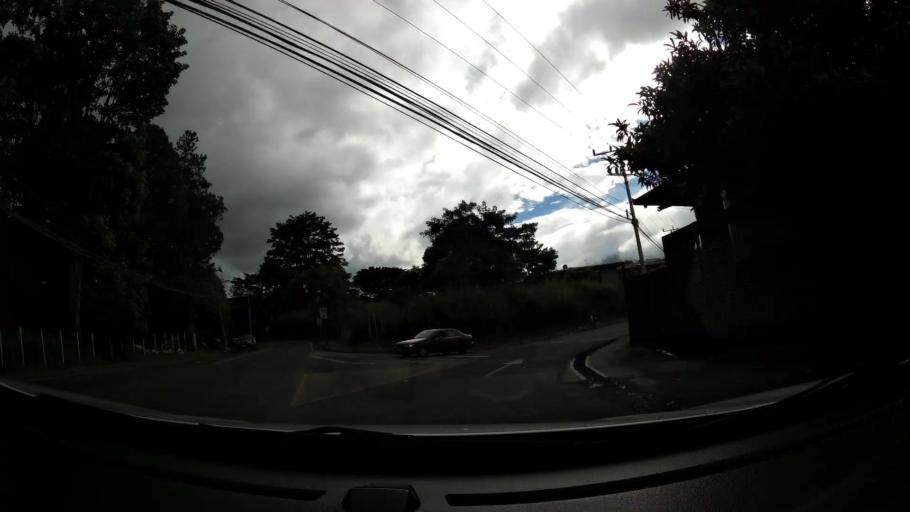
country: CR
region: San Jose
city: Curridabat
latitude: 9.9117
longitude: -84.0435
